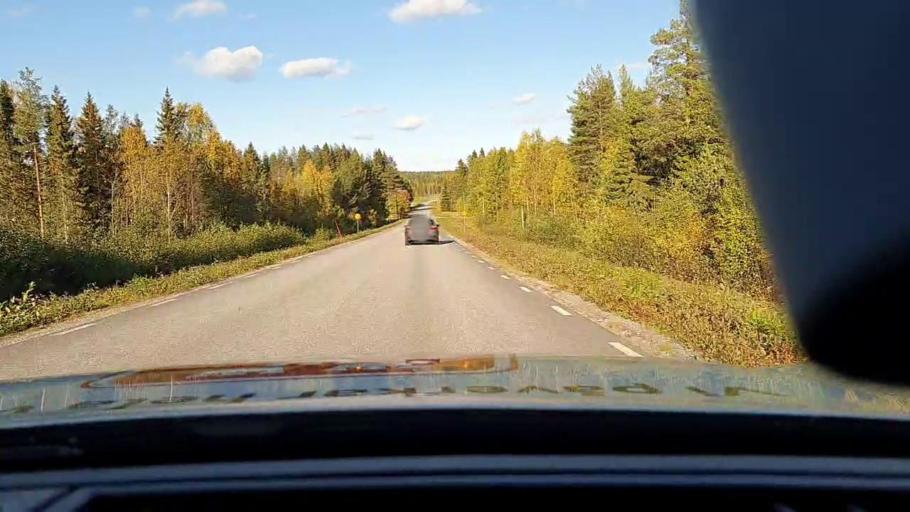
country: SE
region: Norrbotten
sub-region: Pitea Kommun
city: Norrfjarden
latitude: 65.5075
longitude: 21.4838
